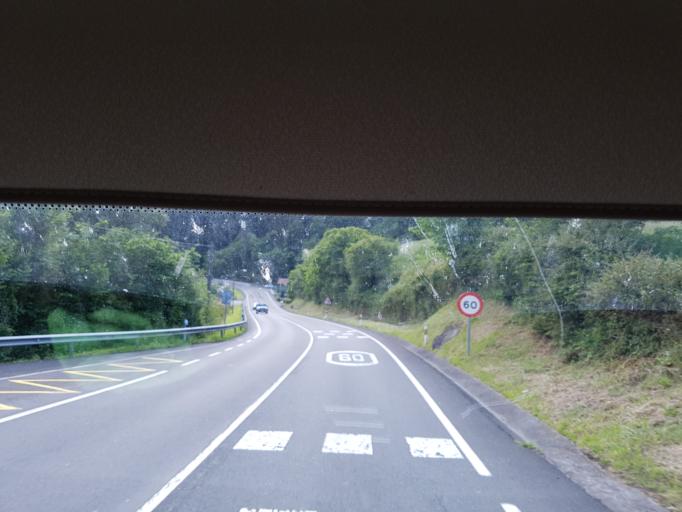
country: ES
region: Basque Country
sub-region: Bizkaia
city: San Julian de Muskiz
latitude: 43.3000
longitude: -3.1239
